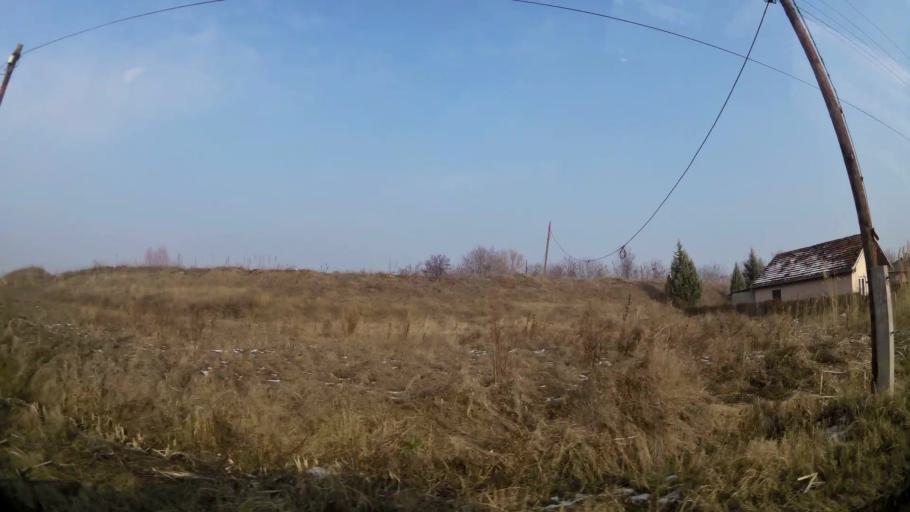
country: MK
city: Kadino
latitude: 41.9790
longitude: 21.5986
